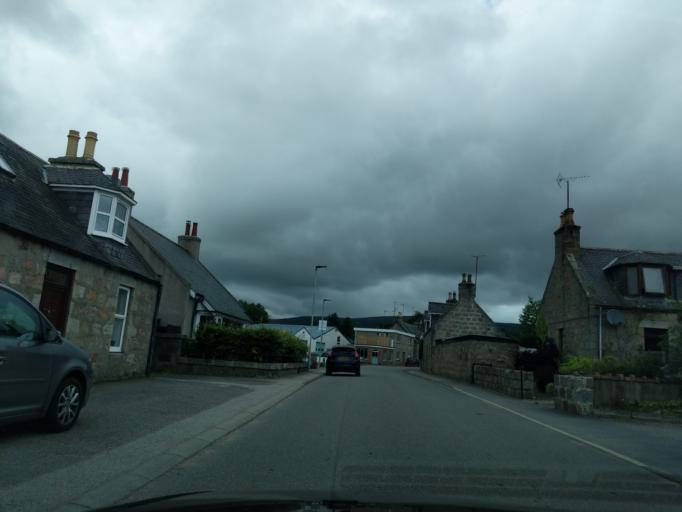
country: GB
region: Scotland
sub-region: Aberdeenshire
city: Aboyne
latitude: 57.1281
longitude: -2.8603
